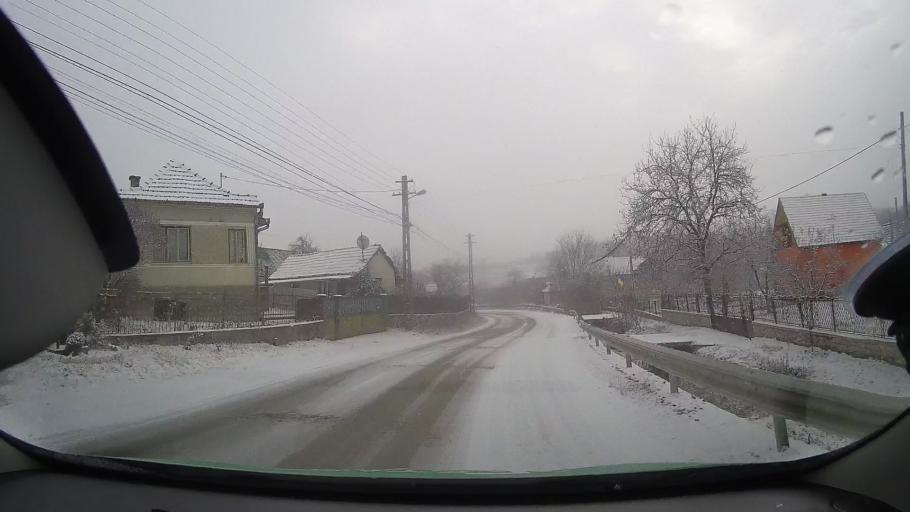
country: RO
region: Alba
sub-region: Comuna Livezile
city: Livezile
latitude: 46.3447
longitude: 23.6554
